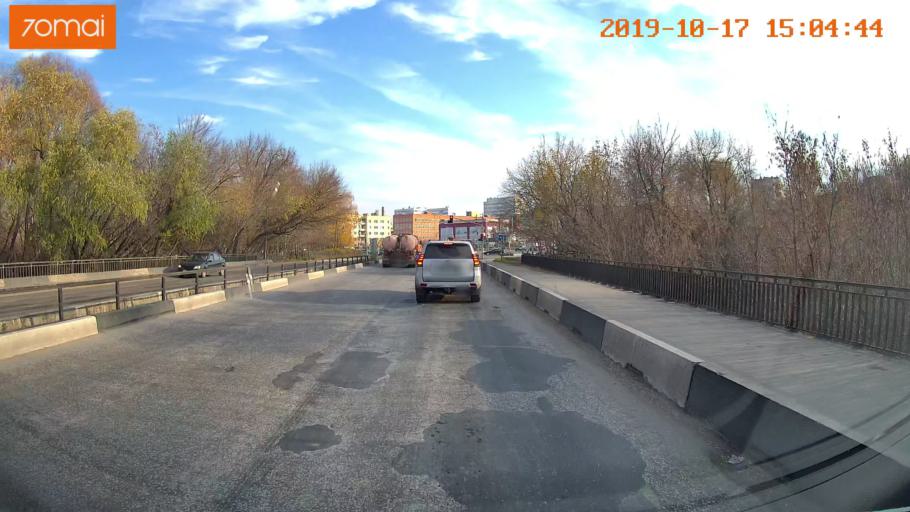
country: RU
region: Rjazan
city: Ryazan'
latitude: 54.6379
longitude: 39.7218
